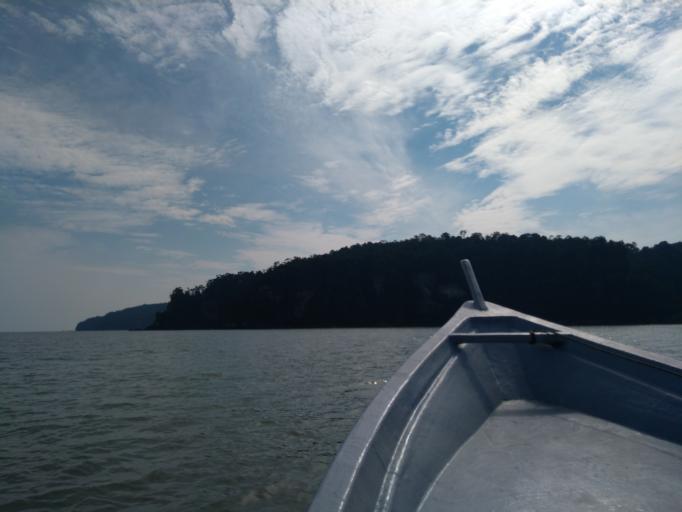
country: MY
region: Sarawak
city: Kuching
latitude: 1.7106
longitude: 110.4364
